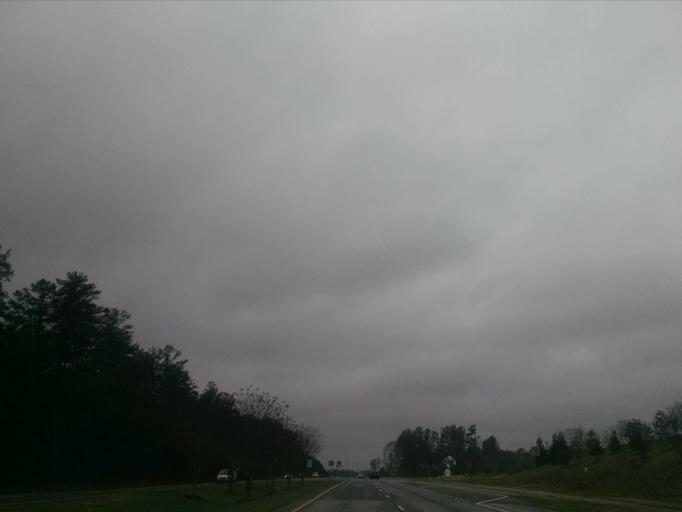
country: US
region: Georgia
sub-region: Gwinnett County
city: Sugar Hill
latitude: 34.0842
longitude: -84.0516
